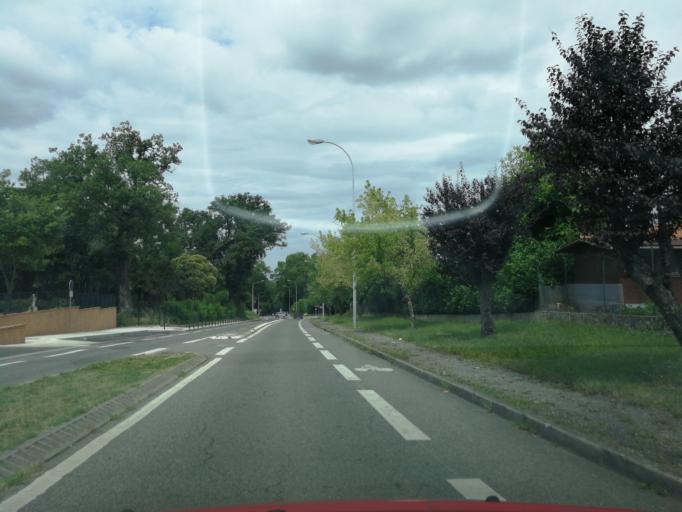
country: FR
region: Midi-Pyrenees
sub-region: Departement de la Haute-Garonne
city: Ramonville-Saint-Agne
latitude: 43.5350
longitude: 1.4710
